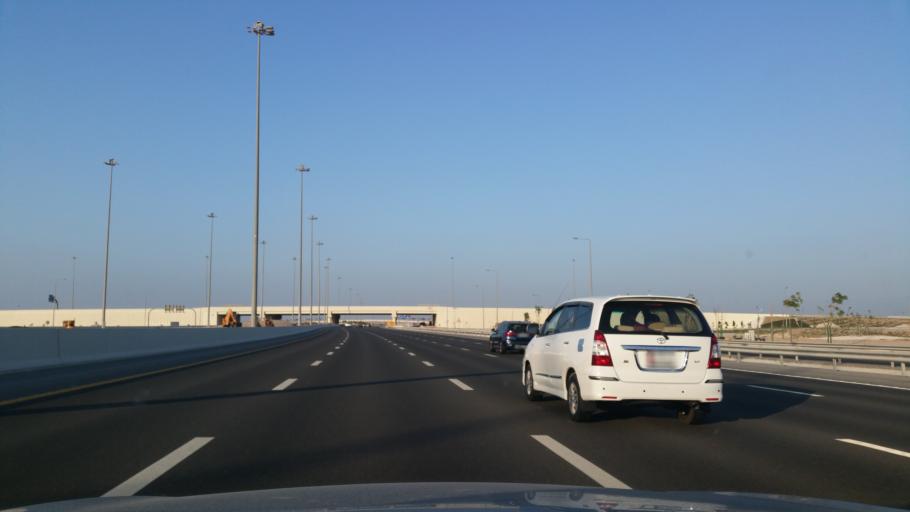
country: QA
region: Al Khawr
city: Al Khawr
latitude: 25.6375
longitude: 51.4918
